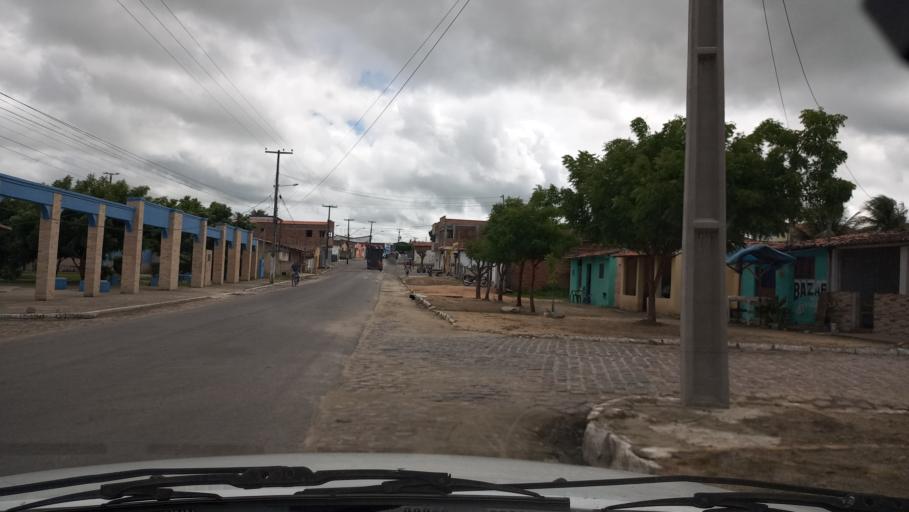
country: BR
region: Rio Grande do Norte
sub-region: Brejinho
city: Brejinho
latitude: -6.1528
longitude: -35.4382
